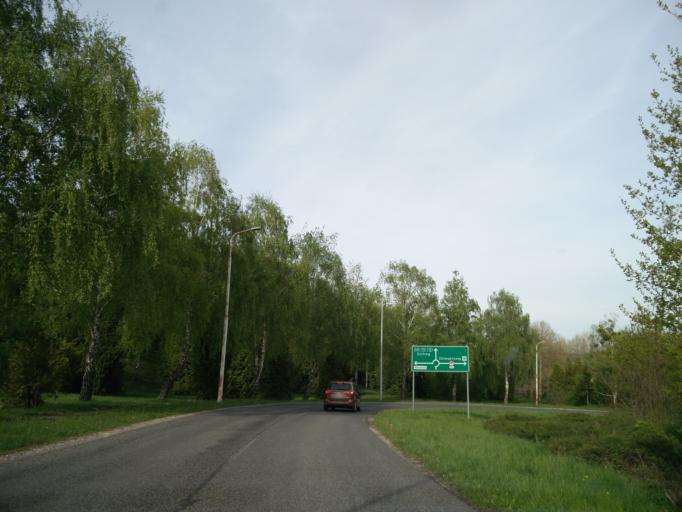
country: HU
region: Zala
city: Zalaegerszeg
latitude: 46.8606
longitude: 16.8483
